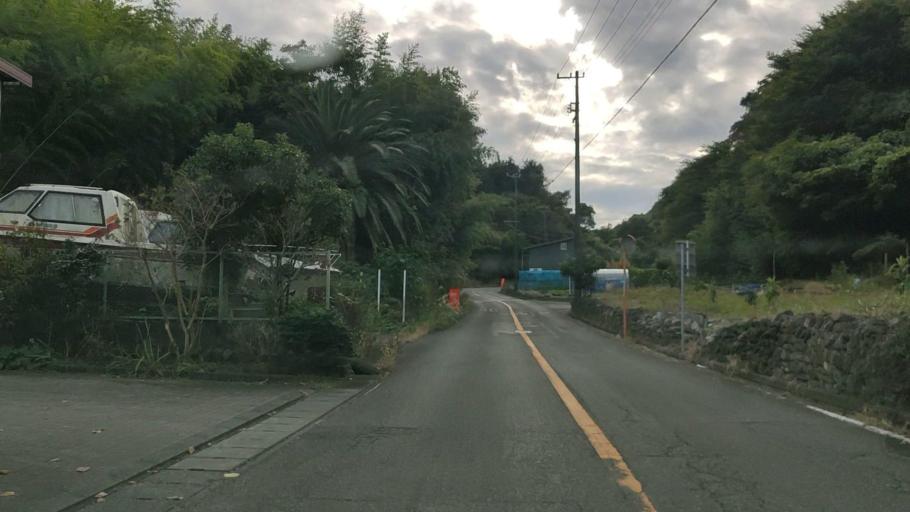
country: JP
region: Shizuoka
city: Shizuoka-shi
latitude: 34.9927
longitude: 138.4668
